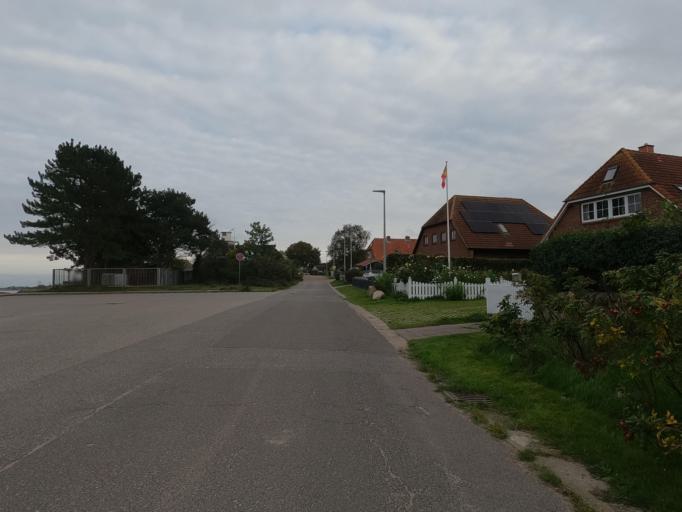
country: DE
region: Schleswig-Holstein
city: Heiligenhafen
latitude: 54.3675
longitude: 11.0195
